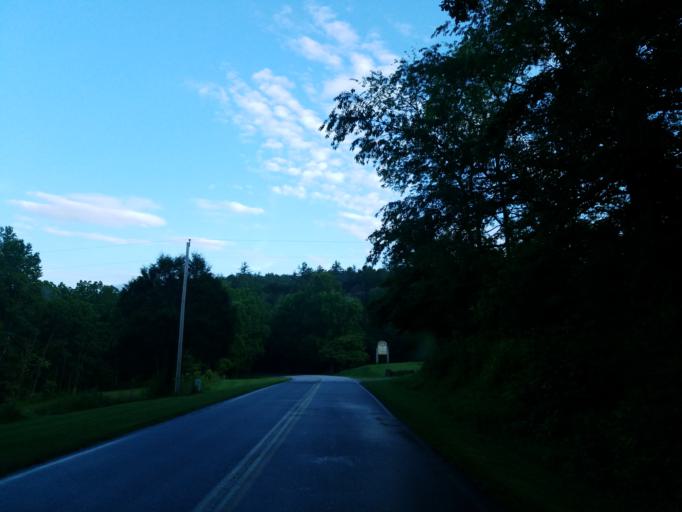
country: US
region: Georgia
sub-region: Fannin County
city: Blue Ridge
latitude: 34.7109
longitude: -84.2355
